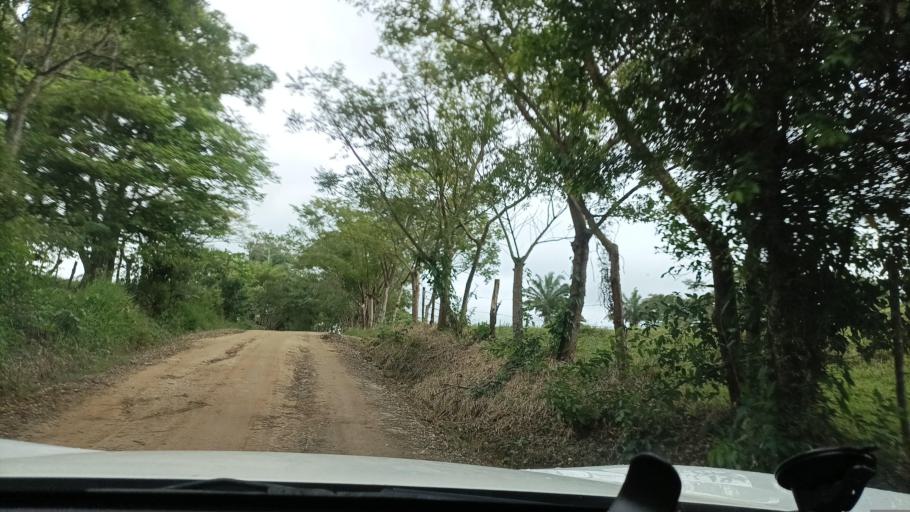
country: MX
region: Veracruz
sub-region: Moloacan
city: Cuichapa
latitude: 17.7886
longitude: -94.3609
